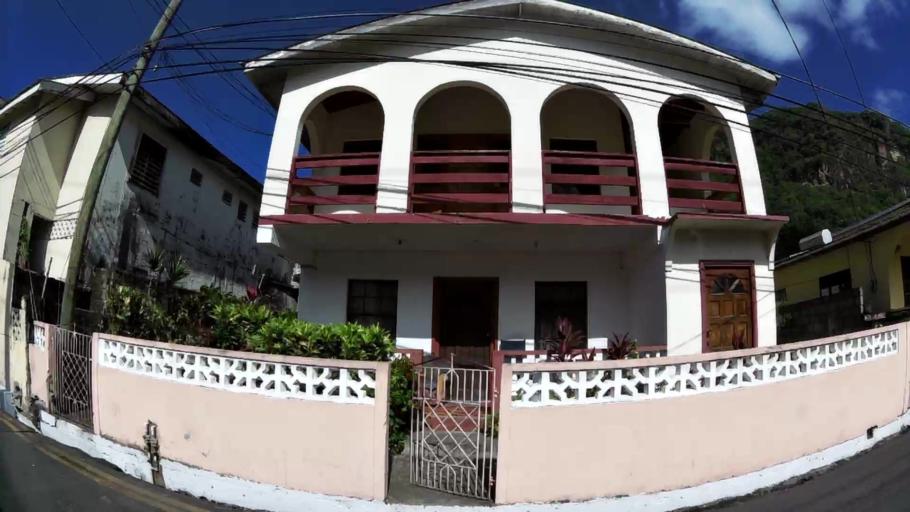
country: LC
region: Soufriere
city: Soufriere
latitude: 13.8567
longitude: -61.0598
